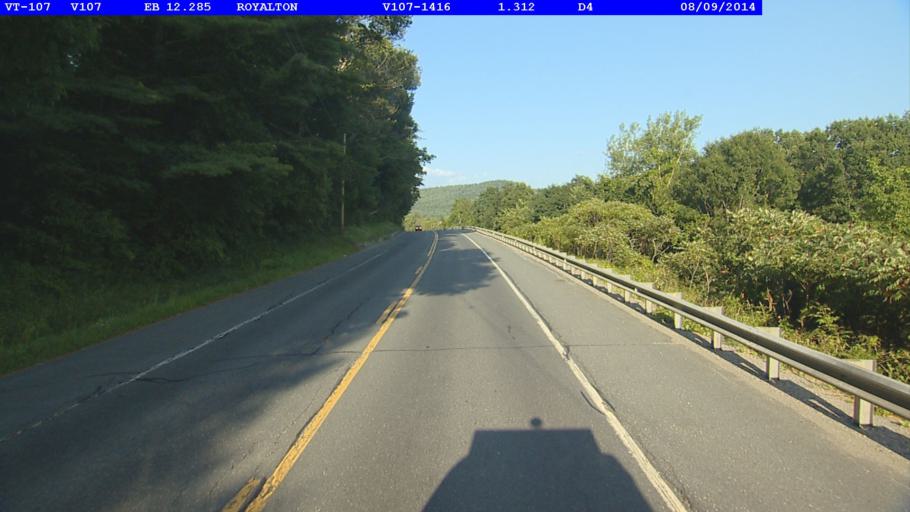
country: US
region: Vermont
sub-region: Orange County
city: Randolph
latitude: 43.8237
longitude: -72.5892
